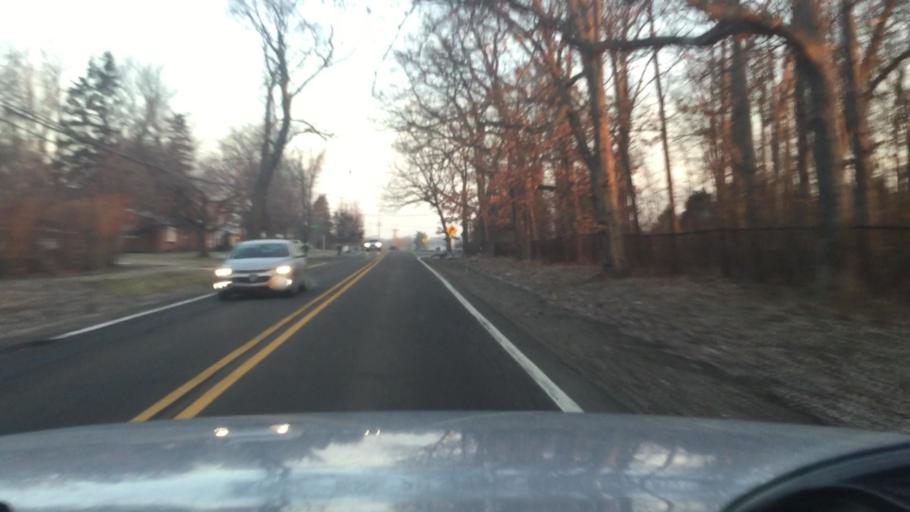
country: US
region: Michigan
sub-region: Oakland County
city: Waterford
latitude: 42.6728
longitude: -83.3572
